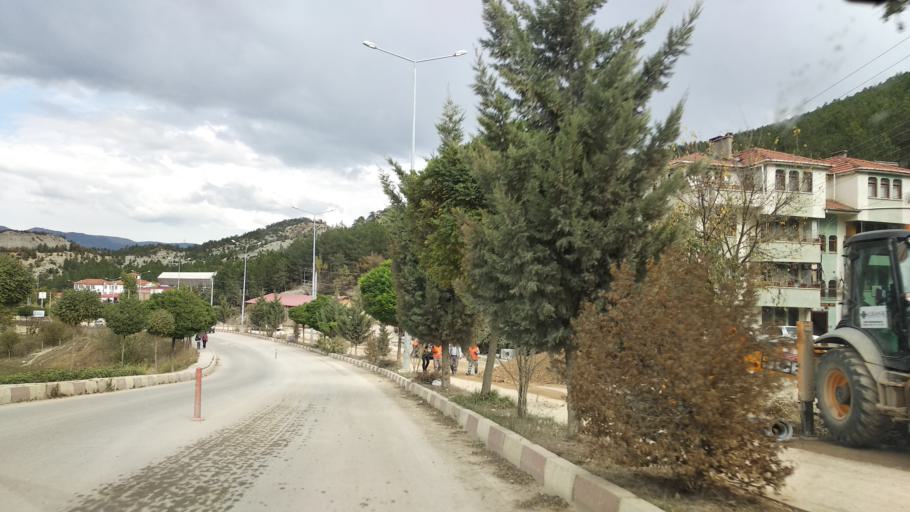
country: TR
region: Bolu
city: Mudurnu
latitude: 40.4751
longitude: 31.2098
